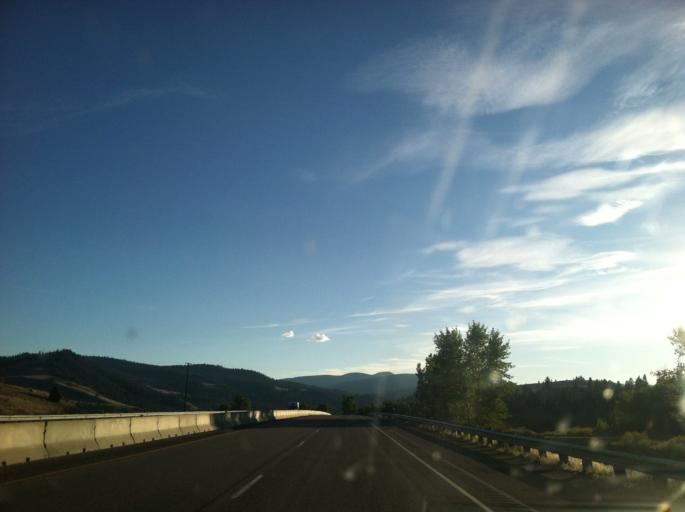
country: US
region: Montana
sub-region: Granite County
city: Philipsburg
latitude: 46.7121
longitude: -113.3299
